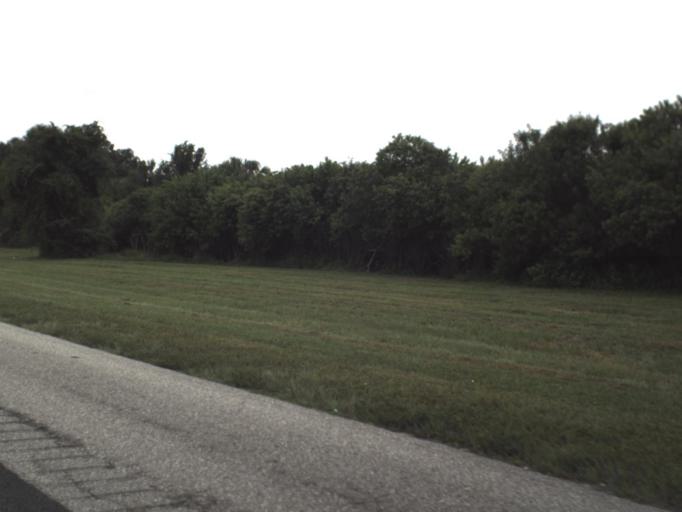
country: US
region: Florida
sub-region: Sarasota County
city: Desoto Lakes
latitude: 27.4476
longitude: -82.4596
